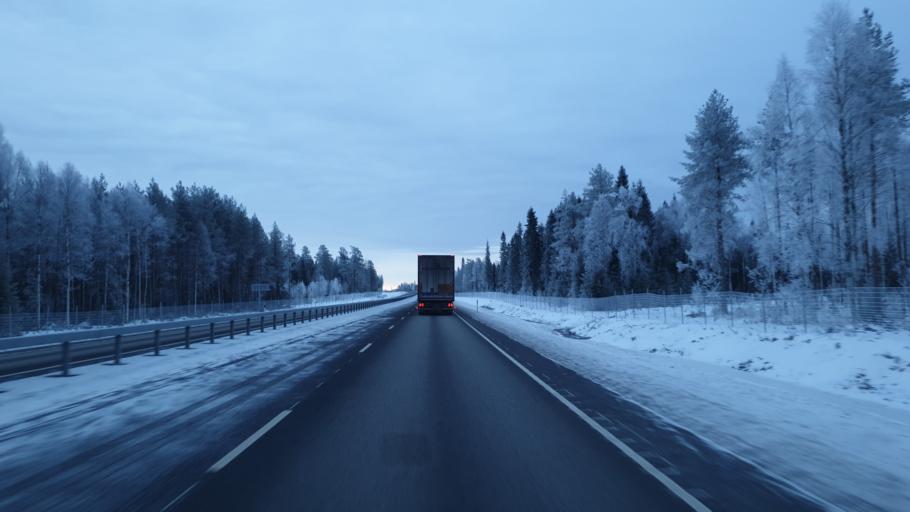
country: FI
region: Lapland
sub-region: Kemi-Tornio
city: Simo
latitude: 65.6351
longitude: 25.1172
